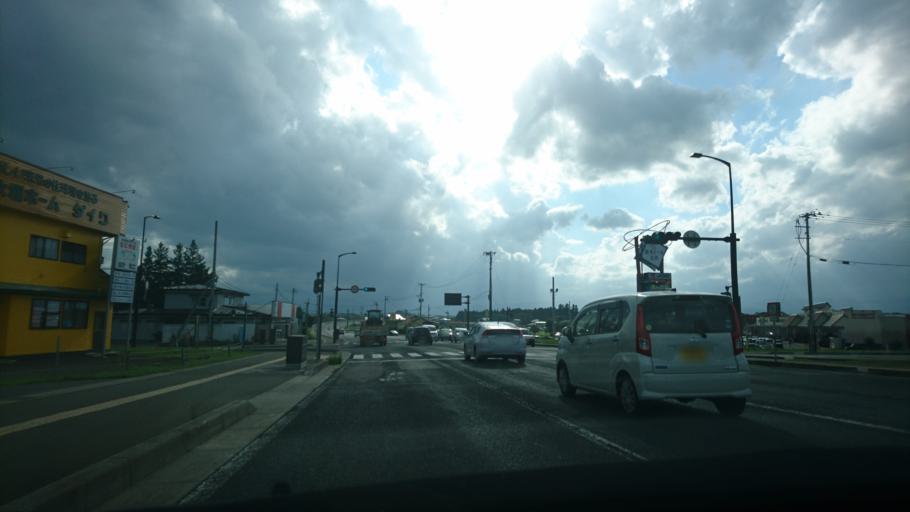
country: JP
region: Iwate
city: Hanamaki
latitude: 39.3857
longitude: 141.1388
